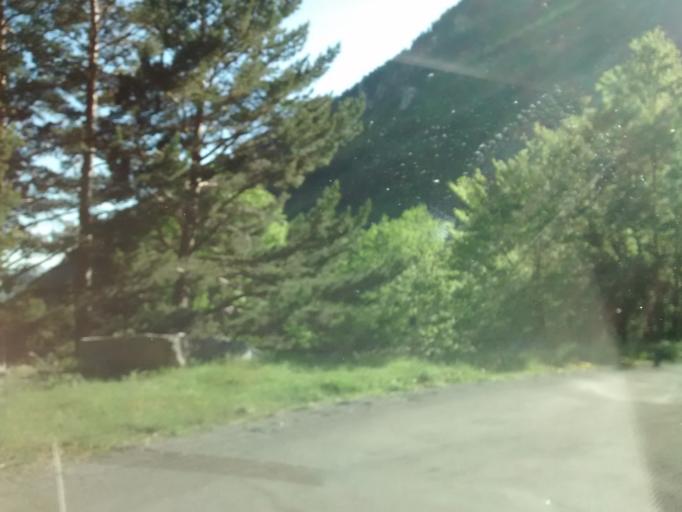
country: ES
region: Aragon
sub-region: Provincia de Huesca
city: Canfranc
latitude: 42.7371
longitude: -0.5917
